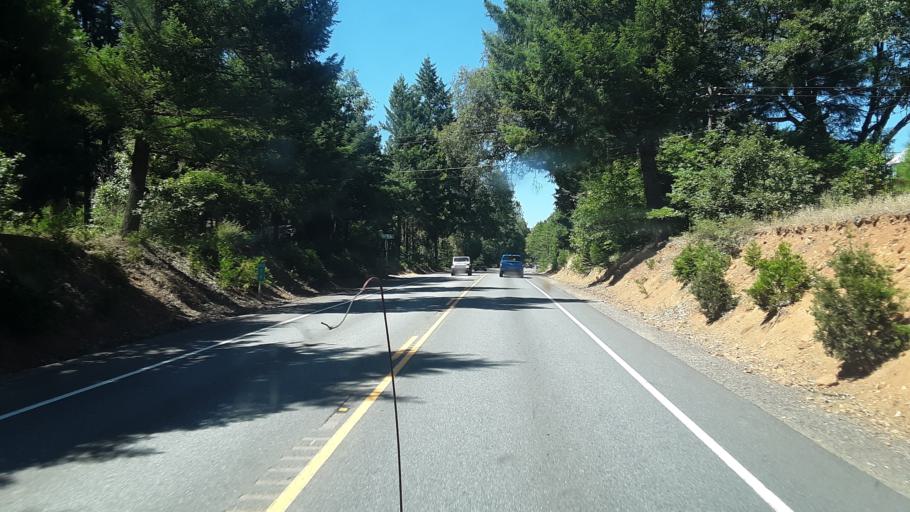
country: US
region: Oregon
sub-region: Josephine County
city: Cave Junction
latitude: 42.2958
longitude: -123.6123
